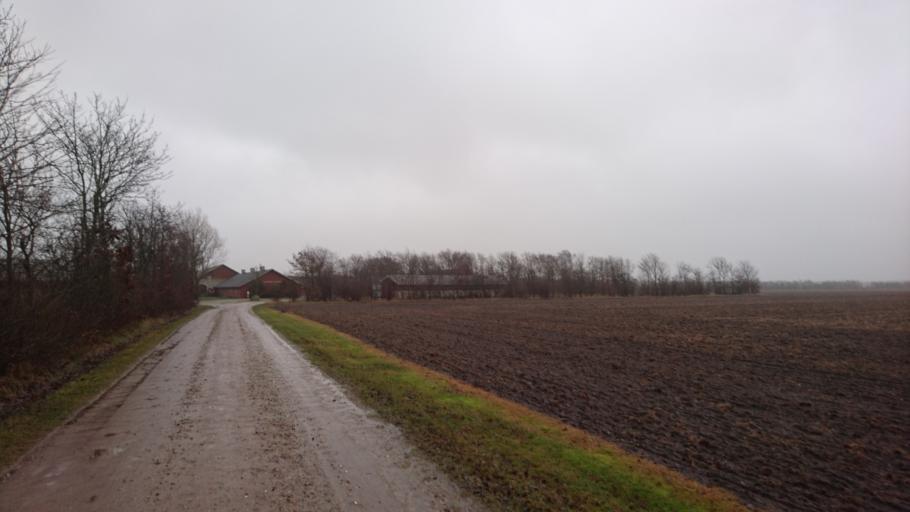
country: DK
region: Central Jutland
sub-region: Herning Kommune
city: Sunds
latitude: 56.1924
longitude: 9.0284
